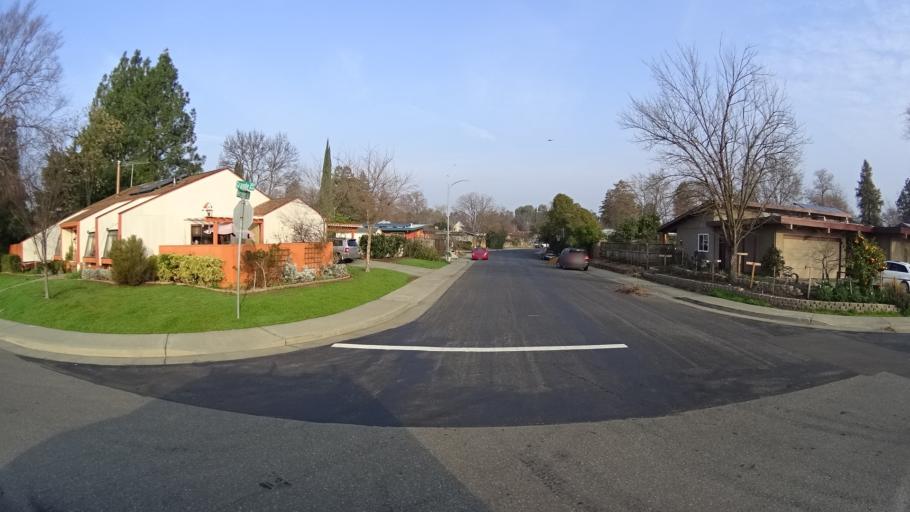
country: US
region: California
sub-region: Yolo County
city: Davis
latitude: 38.5684
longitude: -121.7511
